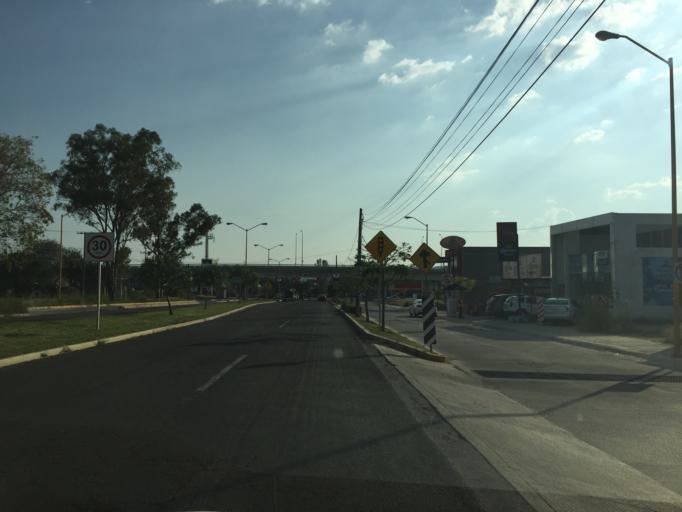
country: MX
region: Aguascalientes
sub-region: Aguascalientes
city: La Loma de los Negritos
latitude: 21.8534
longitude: -102.3520
